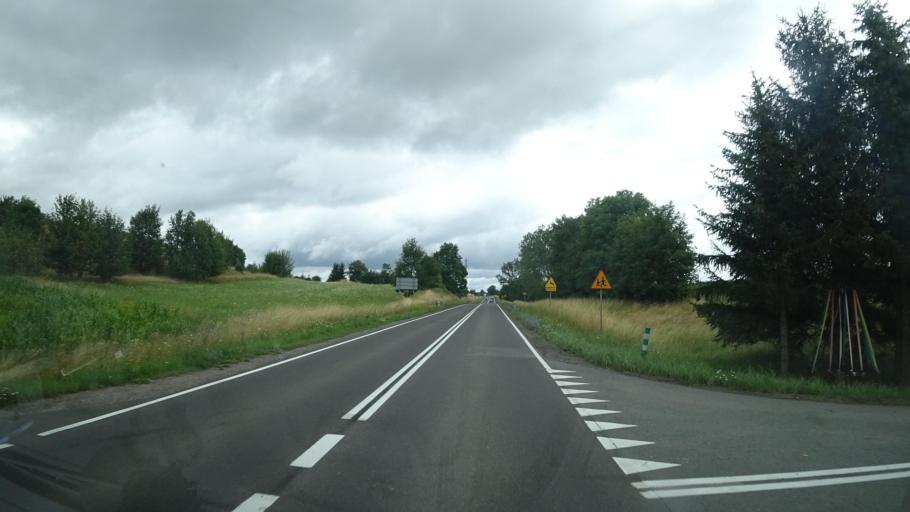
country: PL
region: Warmian-Masurian Voivodeship
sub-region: Powiat elcki
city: Elk
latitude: 53.8047
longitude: 22.2565
